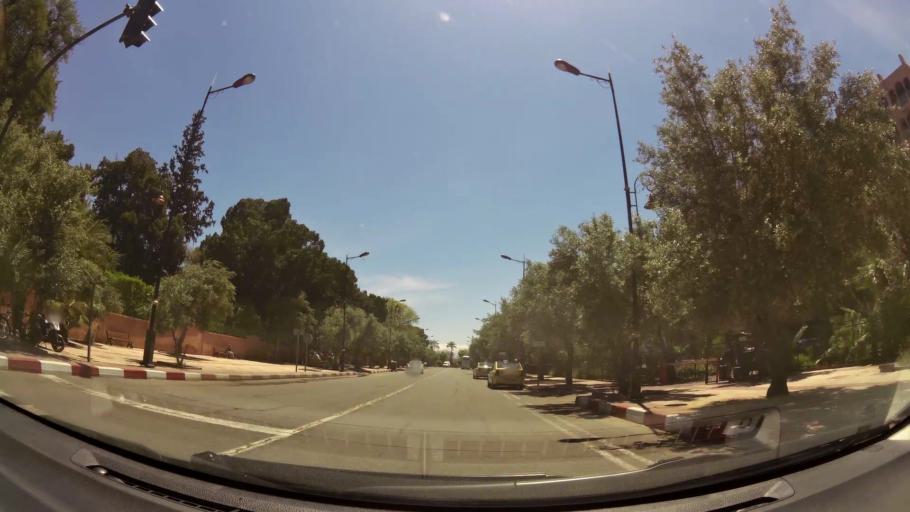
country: MA
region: Marrakech-Tensift-Al Haouz
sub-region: Marrakech
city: Marrakesh
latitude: 31.6213
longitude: -8.0069
